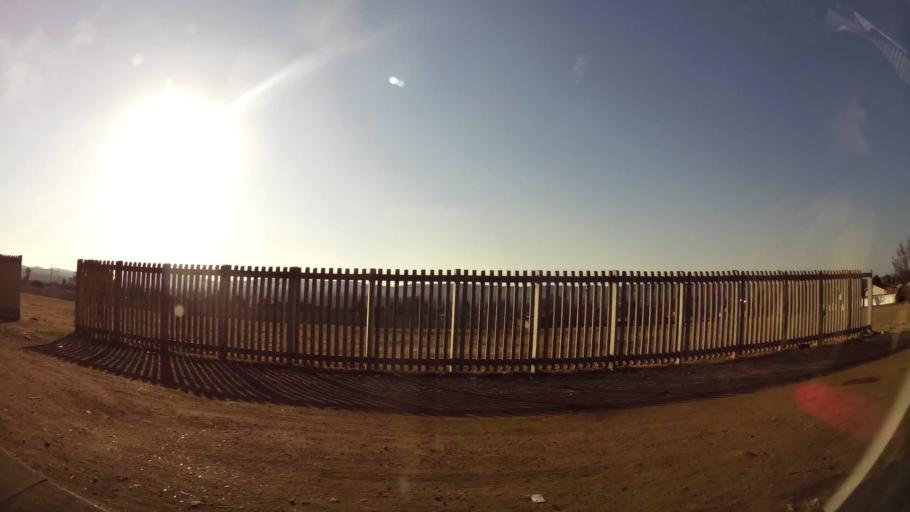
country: ZA
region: Gauteng
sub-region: City of Tshwane Metropolitan Municipality
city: Pretoria
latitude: -25.7554
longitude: 28.1162
